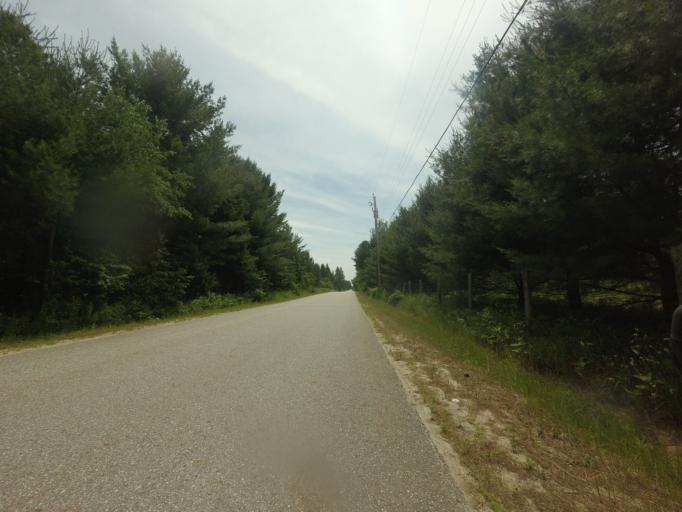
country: CA
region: Quebec
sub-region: Outaouais
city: Wakefield
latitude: 45.9543
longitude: -76.0604
